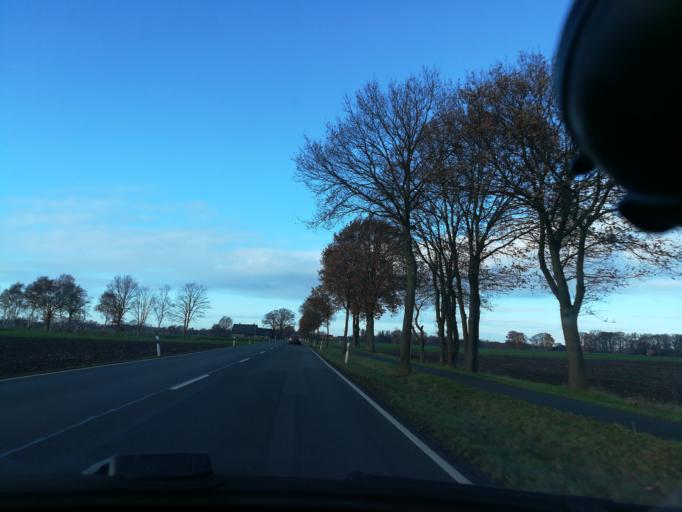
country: DE
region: Lower Saxony
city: Uchte
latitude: 52.4576
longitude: 8.9188
